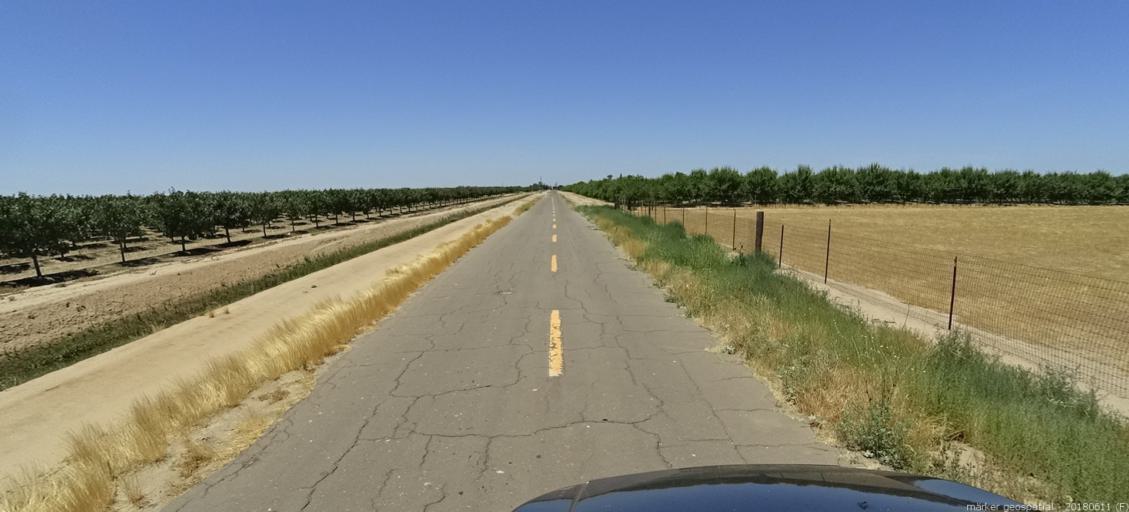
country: US
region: California
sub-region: Madera County
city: Fairmead
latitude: 37.0037
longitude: -120.1857
